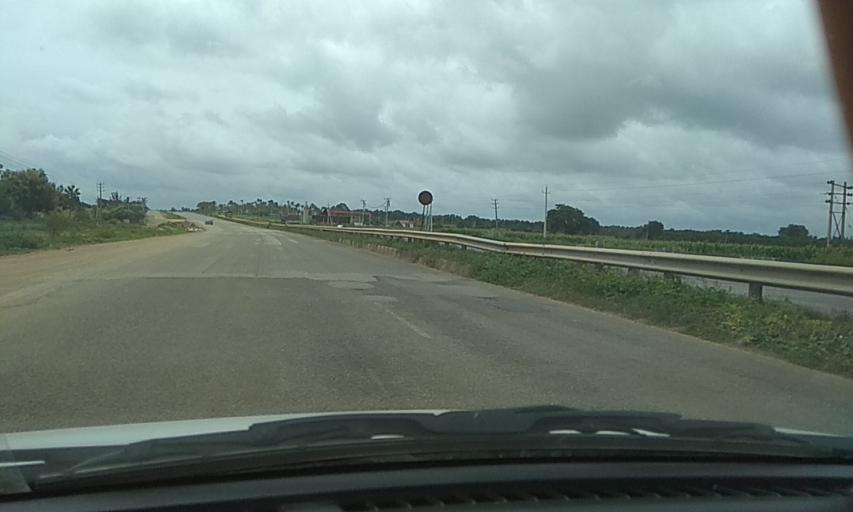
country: IN
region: Karnataka
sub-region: Davanagere
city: Mayakonda
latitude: 14.3592
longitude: 76.1979
